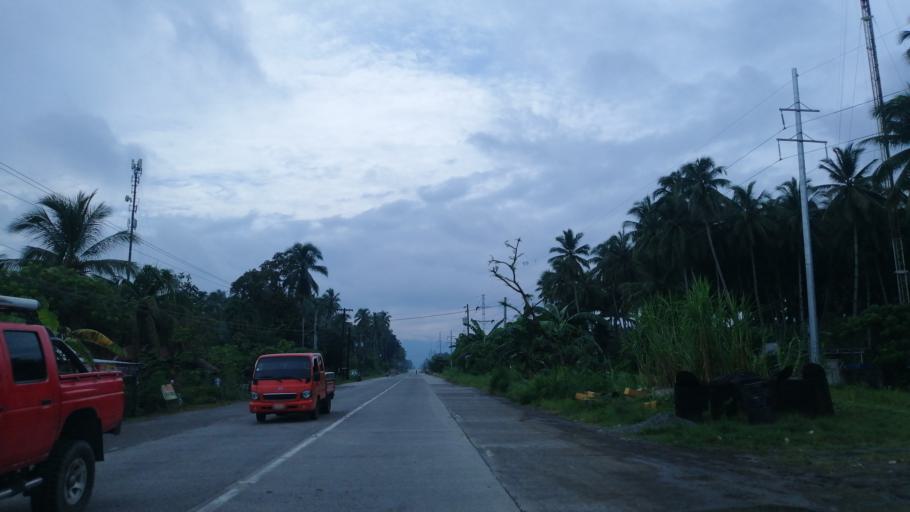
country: PH
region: Davao
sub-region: Province of Davao del Norte
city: Corocotan
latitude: 7.3987
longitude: 125.7743
